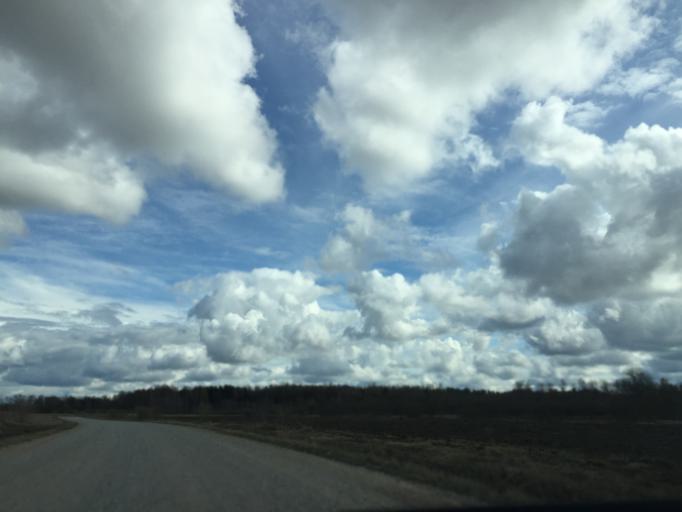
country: LV
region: Limbazu Rajons
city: Limbazi
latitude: 57.6121
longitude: 24.7816
